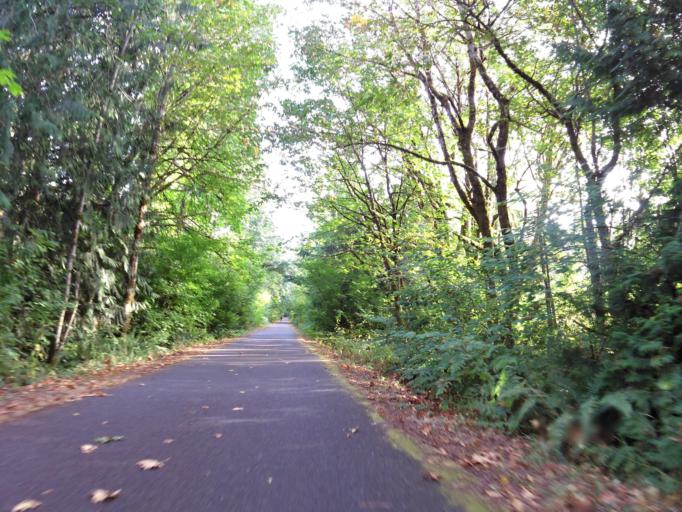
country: US
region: Washington
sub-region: Thurston County
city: Lacey
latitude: 46.9758
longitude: -122.8128
